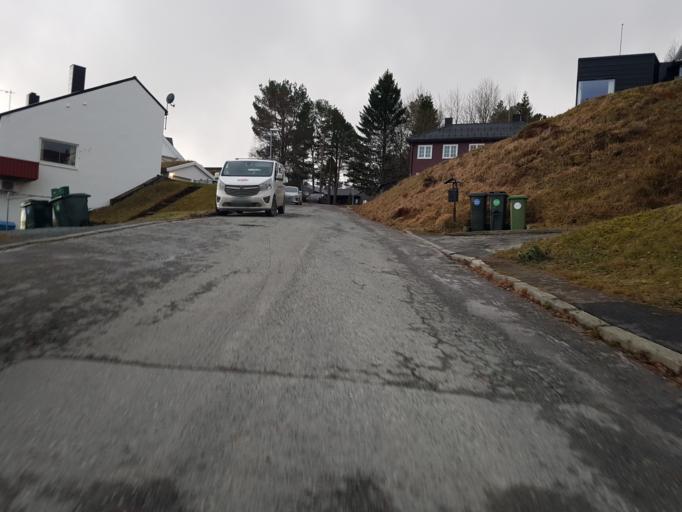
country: NO
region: Sor-Trondelag
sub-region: Trondheim
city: Trondheim
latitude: 63.4120
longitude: 10.3471
